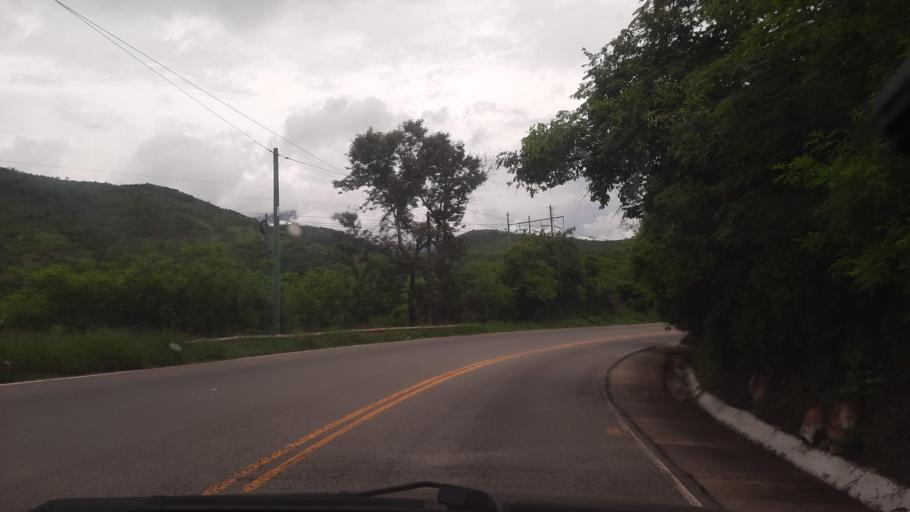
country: GT
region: Chiquimula
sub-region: Municipio de Chiquimula
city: Chiquimula
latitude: 14.8612
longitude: -89.5134
